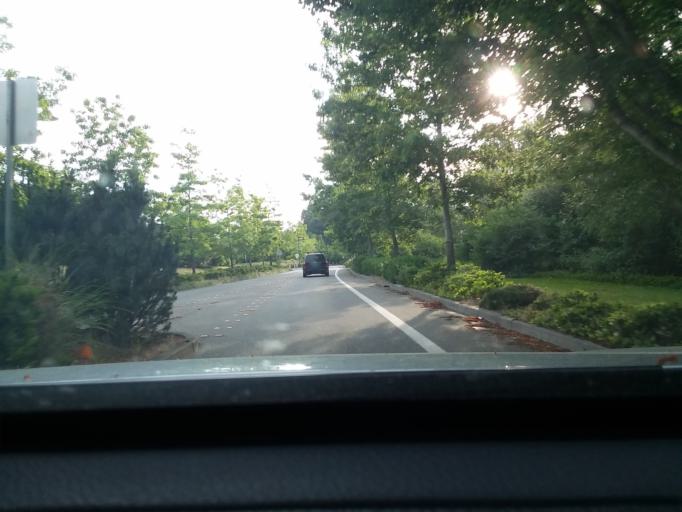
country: US
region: Washington
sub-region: Snohomish County
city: Silver Firs
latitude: 47.8616
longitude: -122.1367
